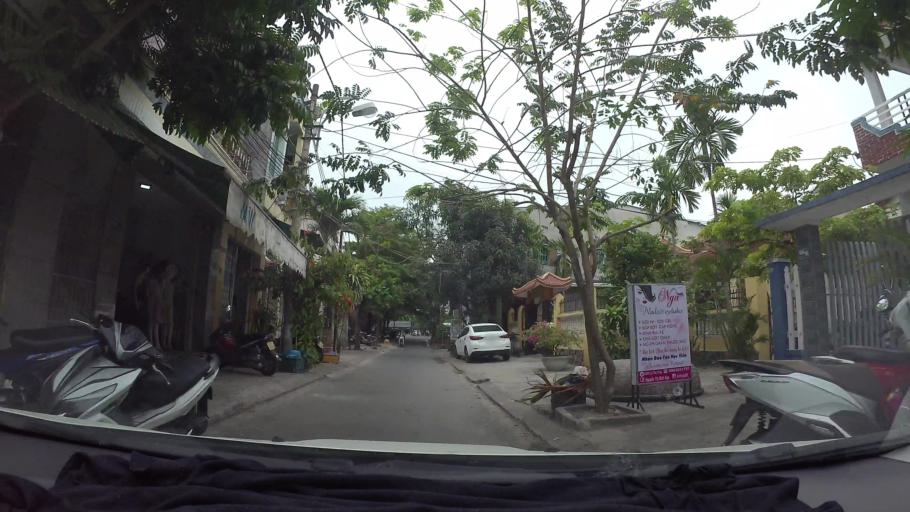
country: VN
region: Da Nang
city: Thanh Khe
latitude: 16.0754
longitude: 108.1753
